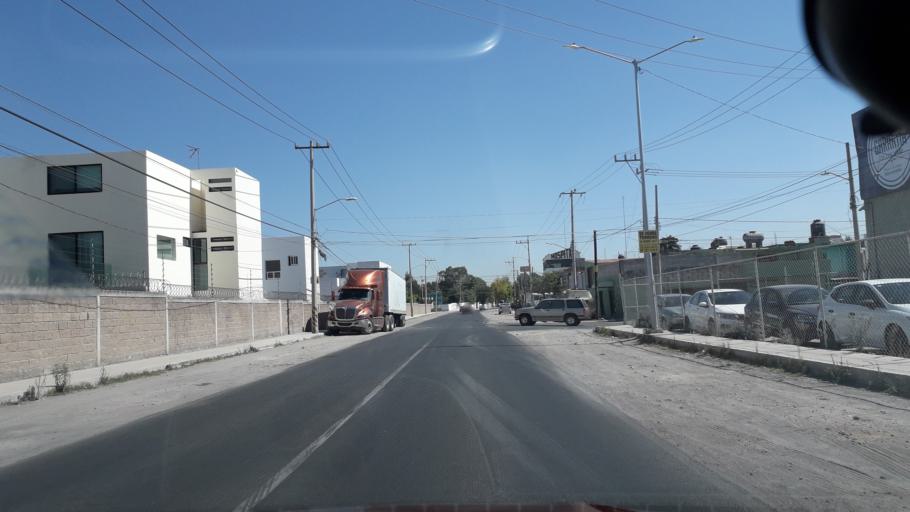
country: MX
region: Puebla
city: Puebla
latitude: 19.0826
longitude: -98.2157
